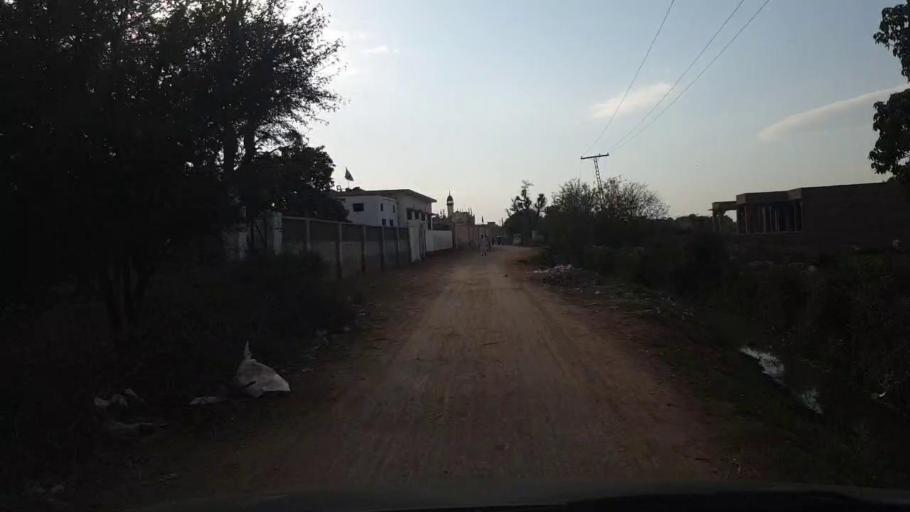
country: PK
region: Sindh
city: Sakrand
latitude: 26.0248
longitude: 68.3748
